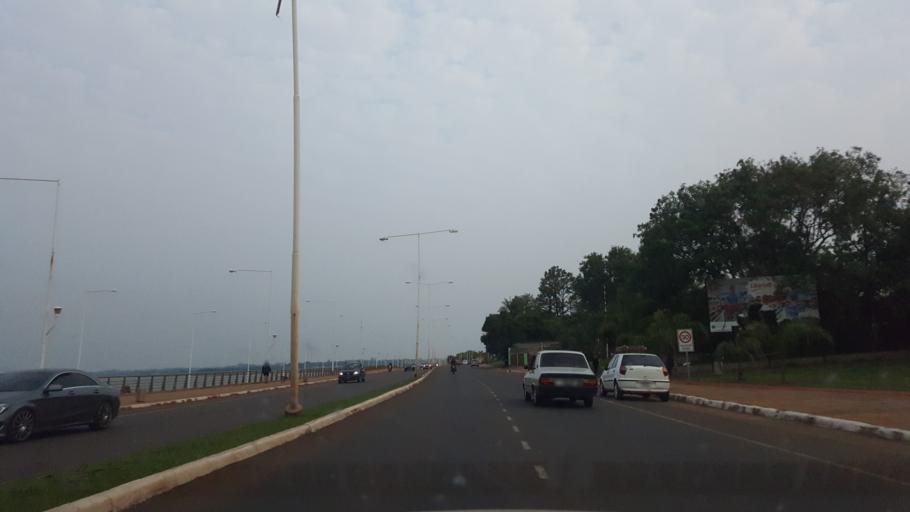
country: AR
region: Misiones
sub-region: Departamento de Capital
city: Posadas
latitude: -27.3958
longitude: -55.8929
